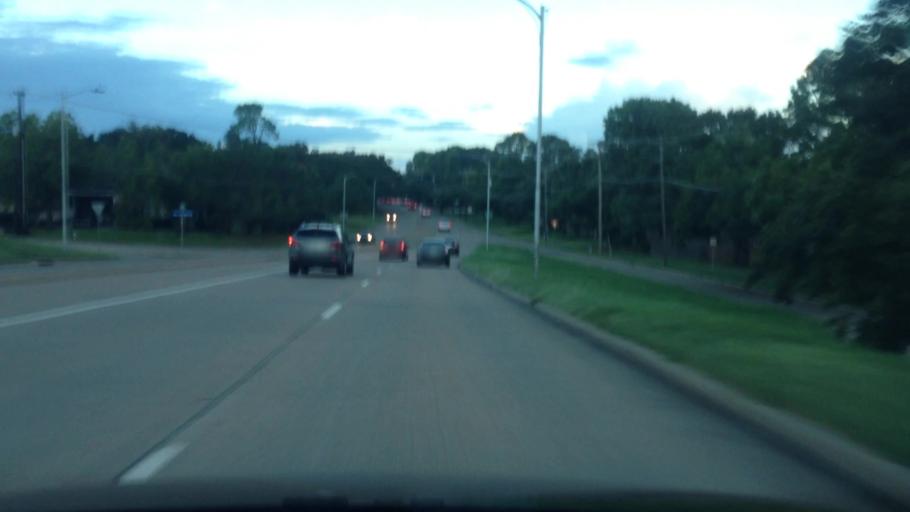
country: US
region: Texas
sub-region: Tarrant County
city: Arlington
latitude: 32.7349
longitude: -97.1317
